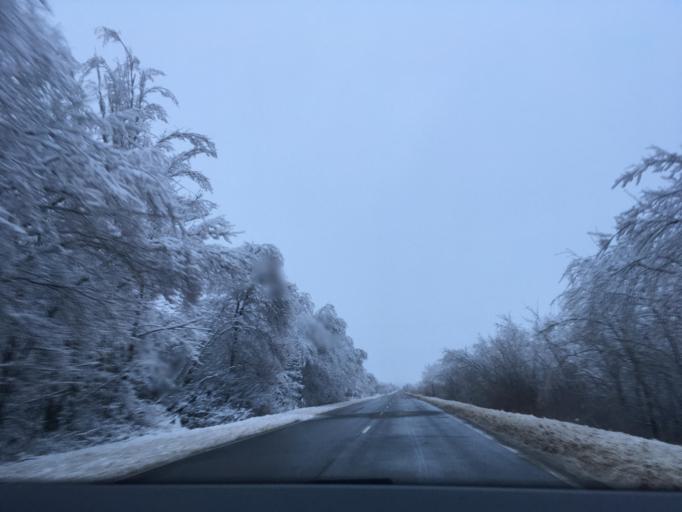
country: RU
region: Voronezj
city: Verkhniy Mamon
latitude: 50.0227
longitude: 40.0862
